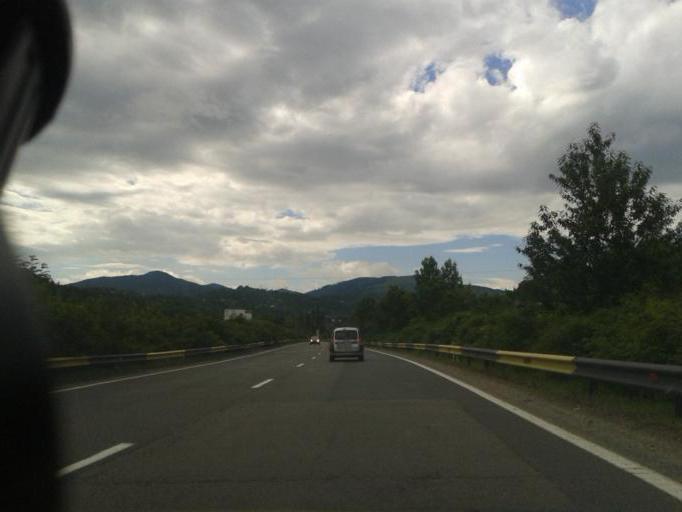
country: RO
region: Prahova
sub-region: Oras Breaza
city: Gura Beliei
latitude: 45.2220
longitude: 25.6442
